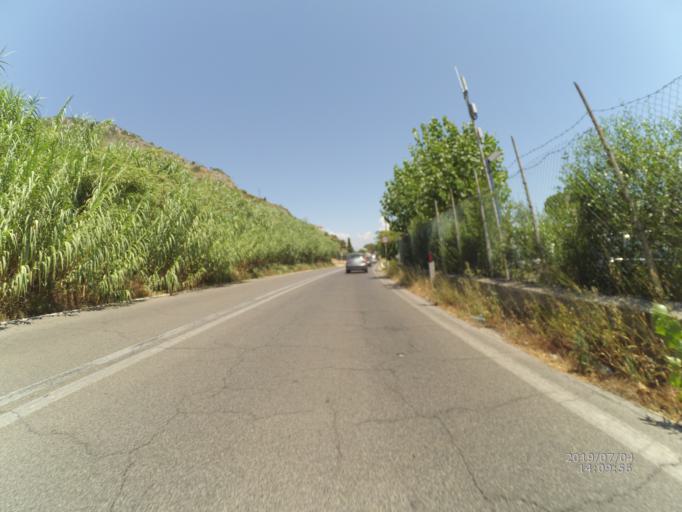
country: IT
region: Latium
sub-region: Provincia di Latina
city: Terracina
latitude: 41.2972
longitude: 13.2711
